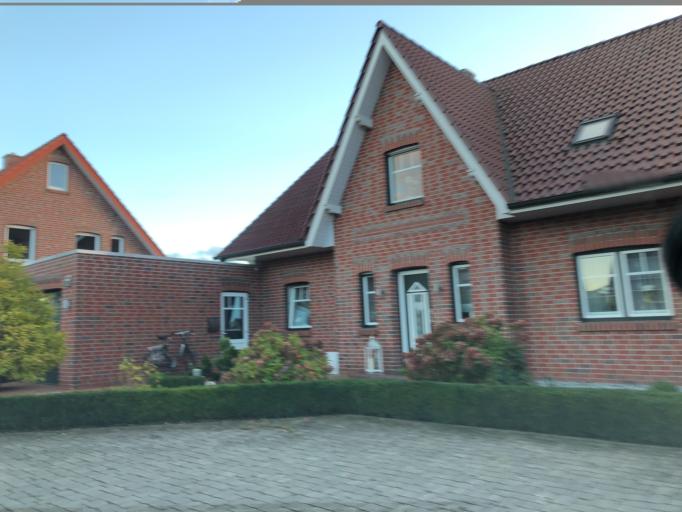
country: DE
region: Lower Saxony
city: Papenburg
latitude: 53.0874
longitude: 7.4256
